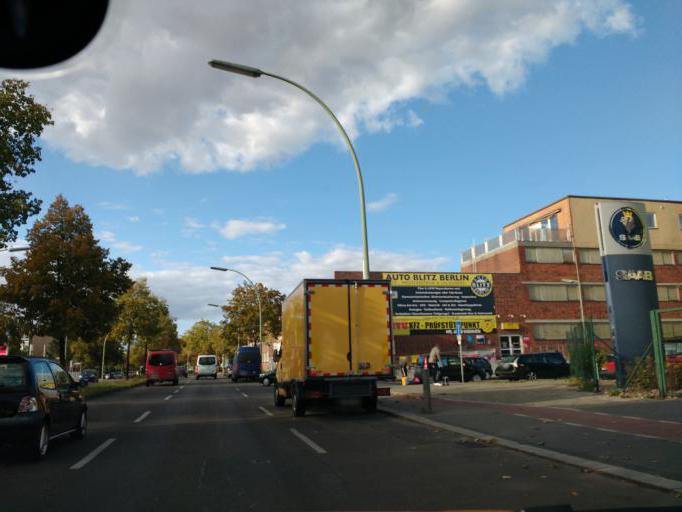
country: DE
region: Berlin
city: Britz
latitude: 52.4502
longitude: 13.4354
